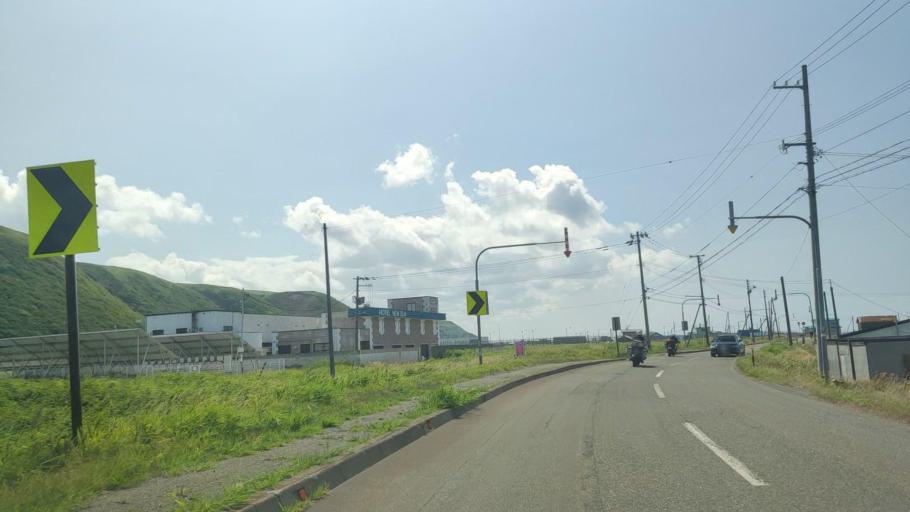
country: JP
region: Hokkaido
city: Wakkanai
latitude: 45.4321
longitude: 141.6397
